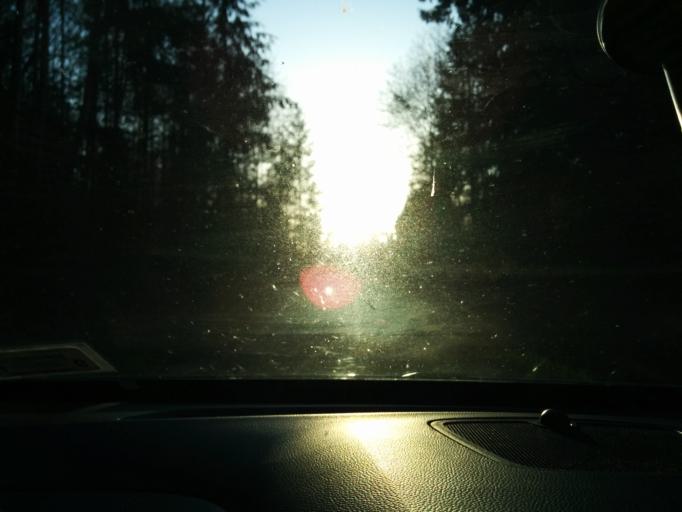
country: US
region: Washington
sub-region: Snohomish County
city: Sultan
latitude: 47.9023
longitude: -121.7769
